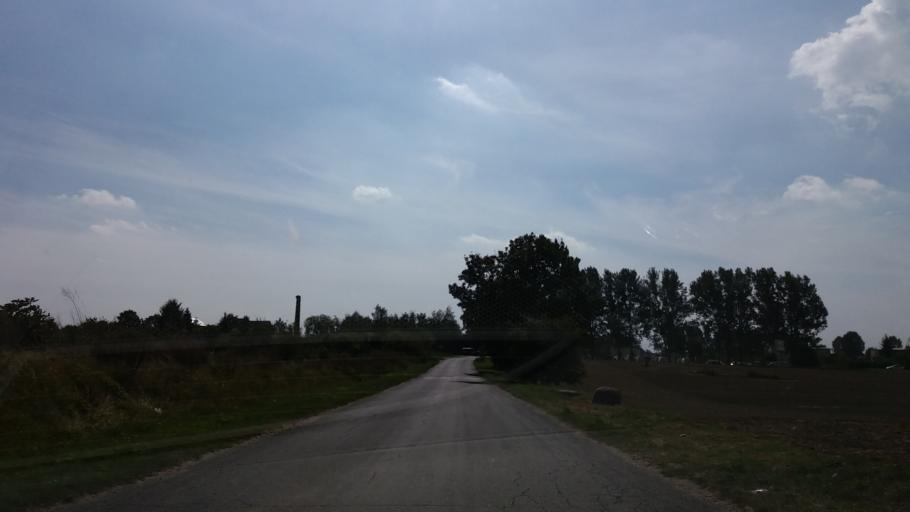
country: PL
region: West Pomeranian Voivodeship
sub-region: Powiat stargardzki
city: Stargard Szczecinski
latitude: 53.3473
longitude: 14.9711
